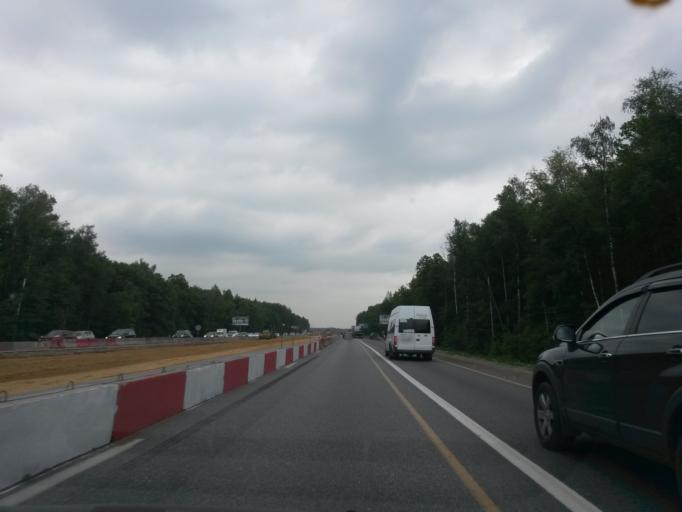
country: RU
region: Moskovskaya
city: Lyubuchany
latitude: 55.2187
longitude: 37.5336
